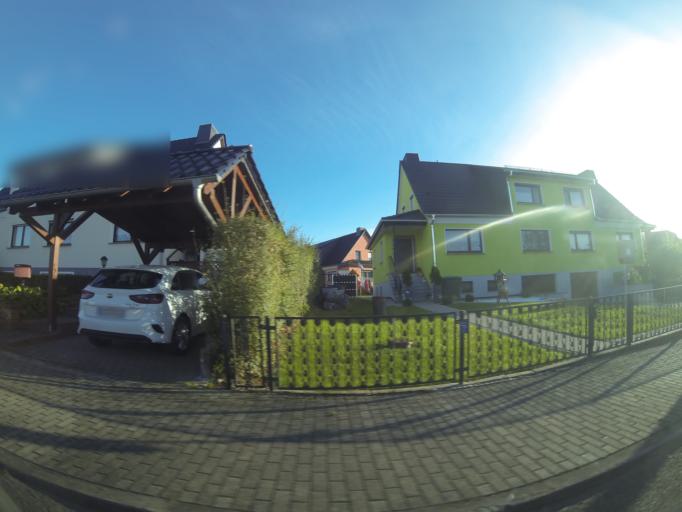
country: DE
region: Thuringia
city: Schmolln
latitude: 50.8926
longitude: 12.3609
